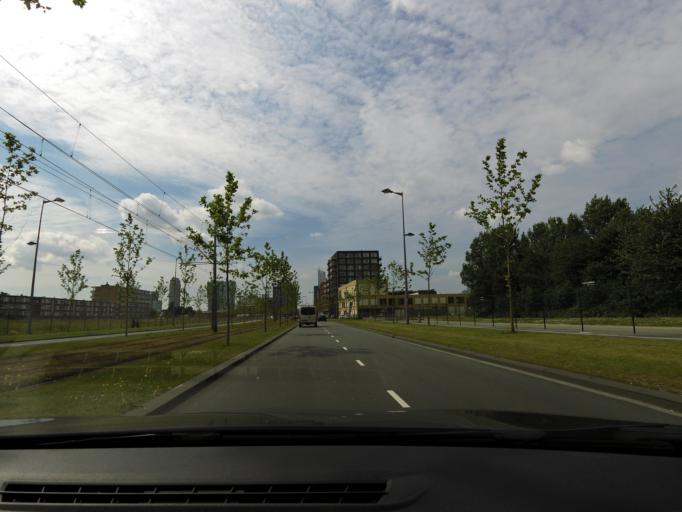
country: NL
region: South Holland
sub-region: Gemeente Rotterdam
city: Rotterdam
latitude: 51.9023
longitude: 4.5078
